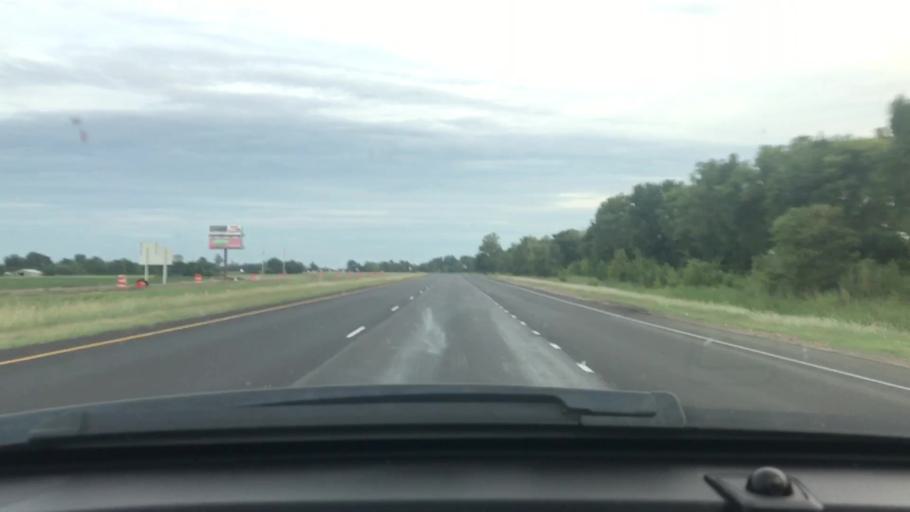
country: US
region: Arkansas
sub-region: Poinsett County
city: Trumann
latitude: 35.6745
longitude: -90.5530
